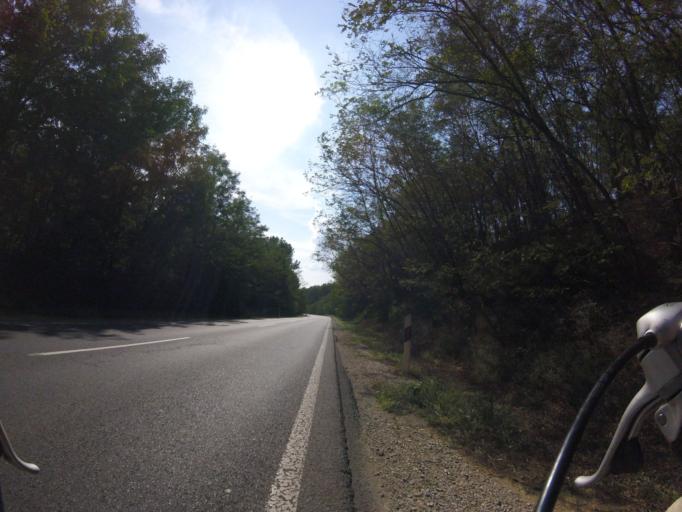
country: HU
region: Szabolcs-Szatmar-Bereg
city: Nyirbogdany
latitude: 48.0547
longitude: 21.9069
